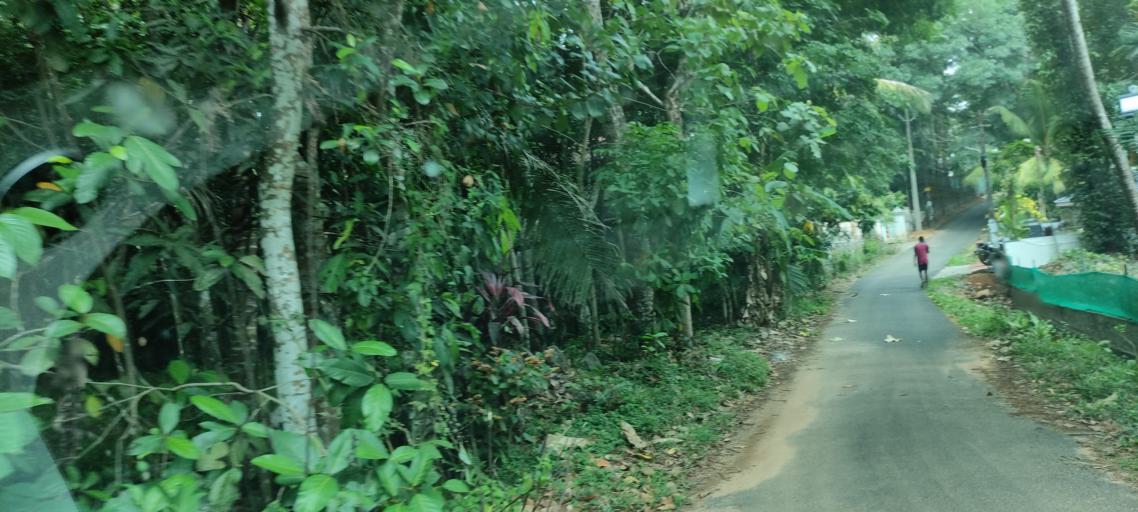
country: IN
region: Kerala
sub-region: Pattanamtitta
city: Adur
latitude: 9.1696
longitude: 76.7444
